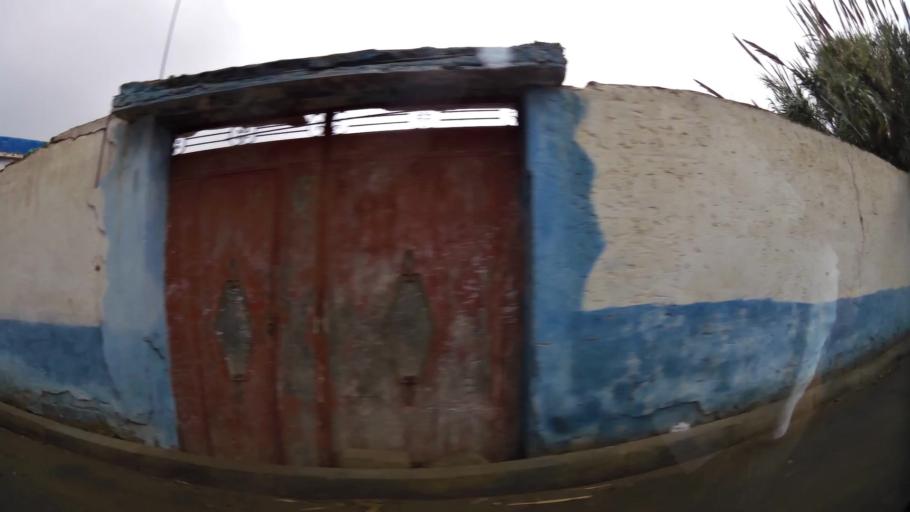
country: MA
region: Oriental
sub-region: Nador
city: Nador
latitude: 35.1585
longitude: -2.9526
